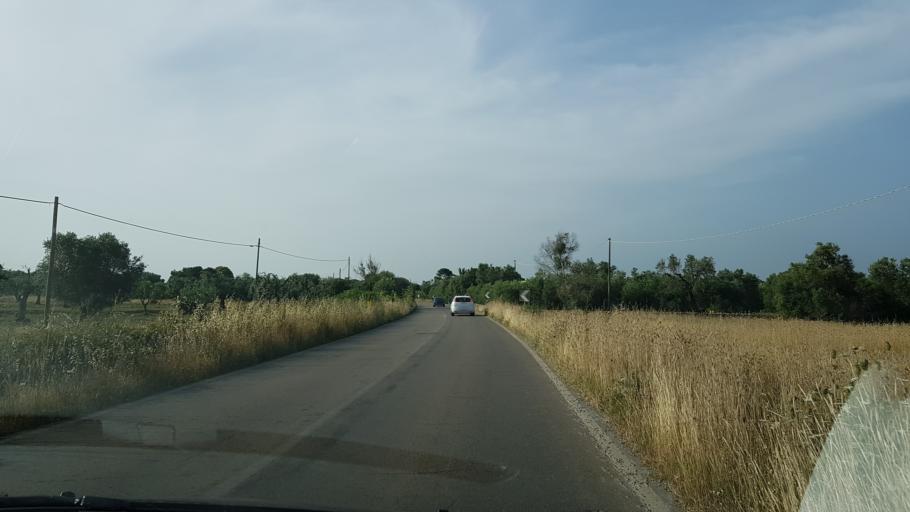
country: IT
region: Apulia
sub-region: Provincia di Lecce
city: Porto Cesareo
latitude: 40.3093
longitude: 17.8634
